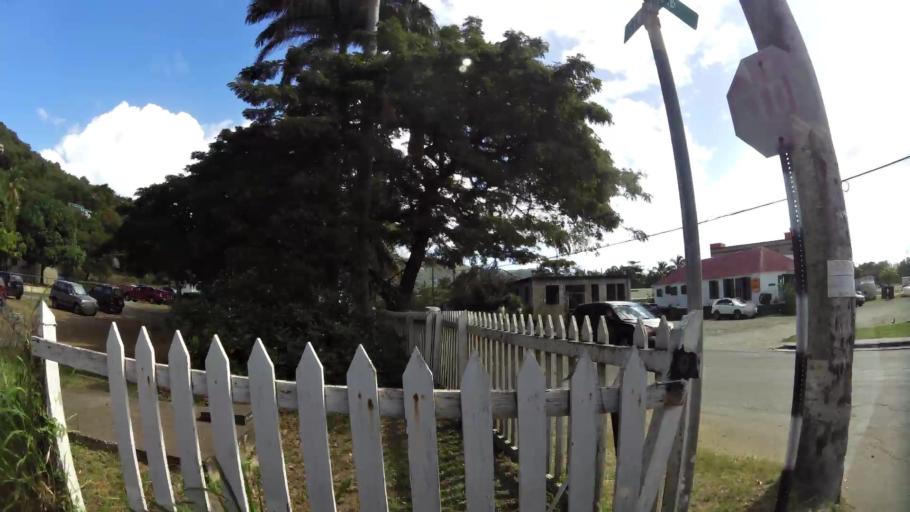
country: VG
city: Road Town
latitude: 18.4273
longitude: -64.6197
